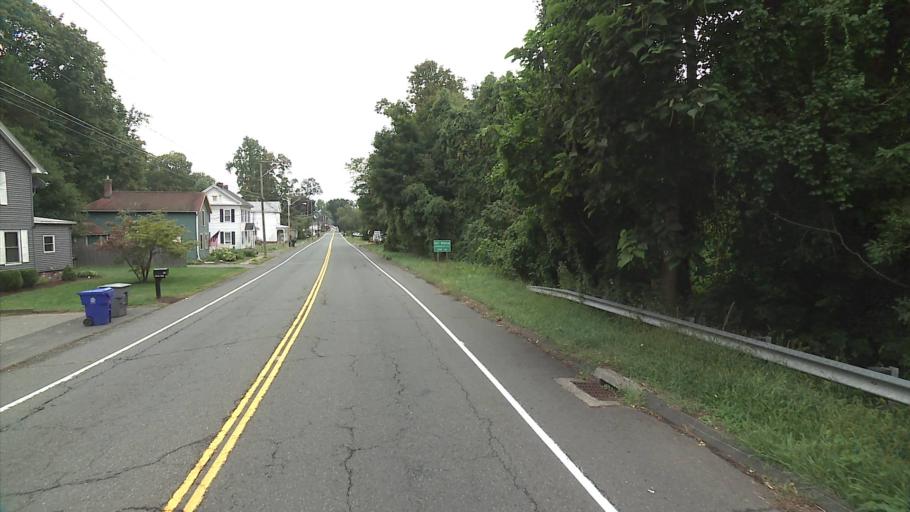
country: US
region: Connecticut
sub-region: Hartford County
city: Windsor Locks
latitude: 41.9353
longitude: -72.6176
